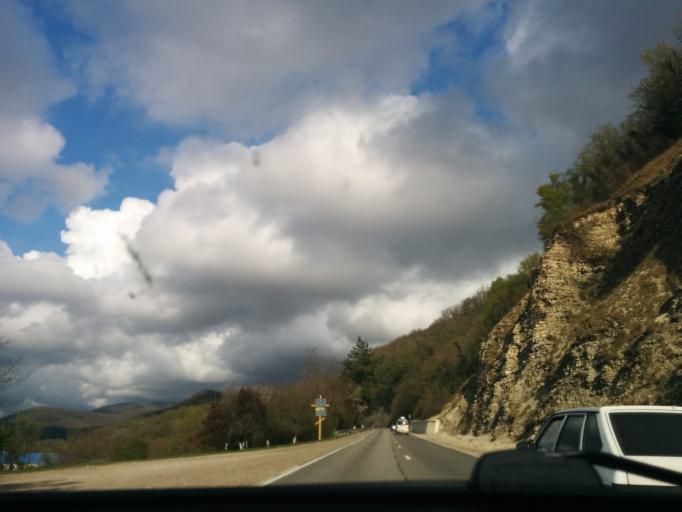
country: RU
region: Krasnodarskiy
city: Novomikhaylovskiy
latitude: 44.2559
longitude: 38.8700
